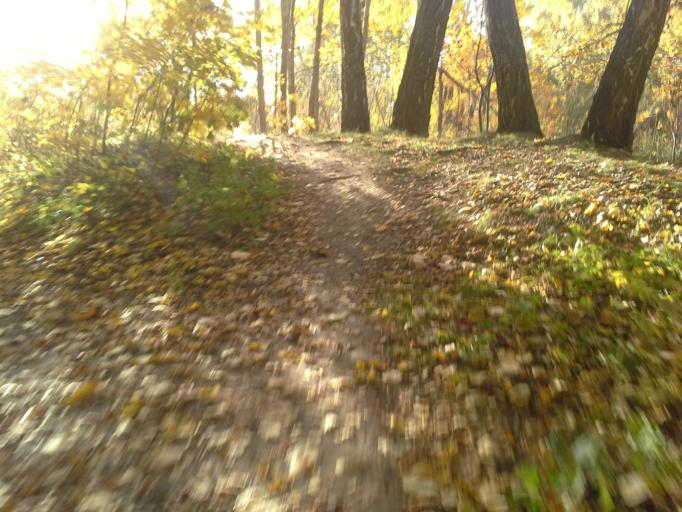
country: RU
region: Moskovskaya
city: Kommunarka
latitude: 55.5621
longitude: 37.5197
